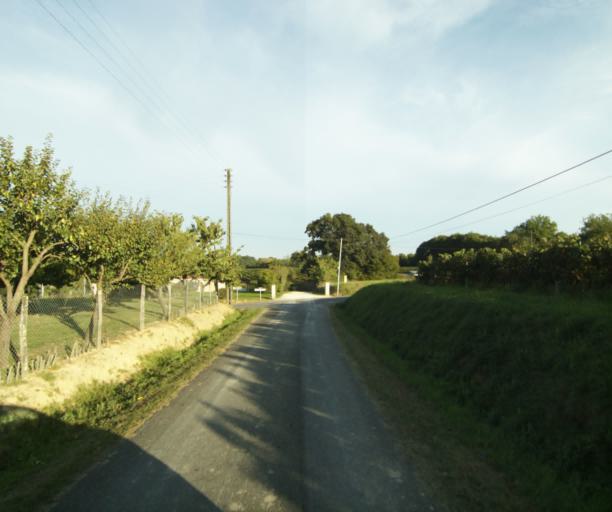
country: FR
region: Midi-Pyrenees
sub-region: Departement du Gers
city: Eauze
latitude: 43.8492
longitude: 0.0200
